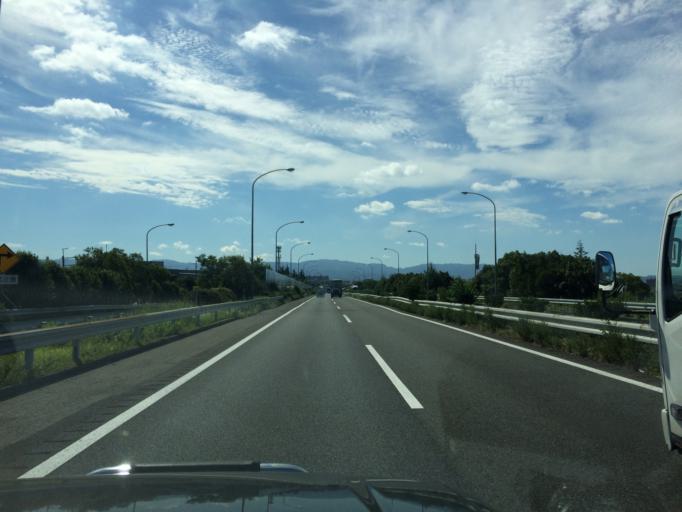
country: JP
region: Osaka
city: Takaishi
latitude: 34.5128
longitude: 135.4899
